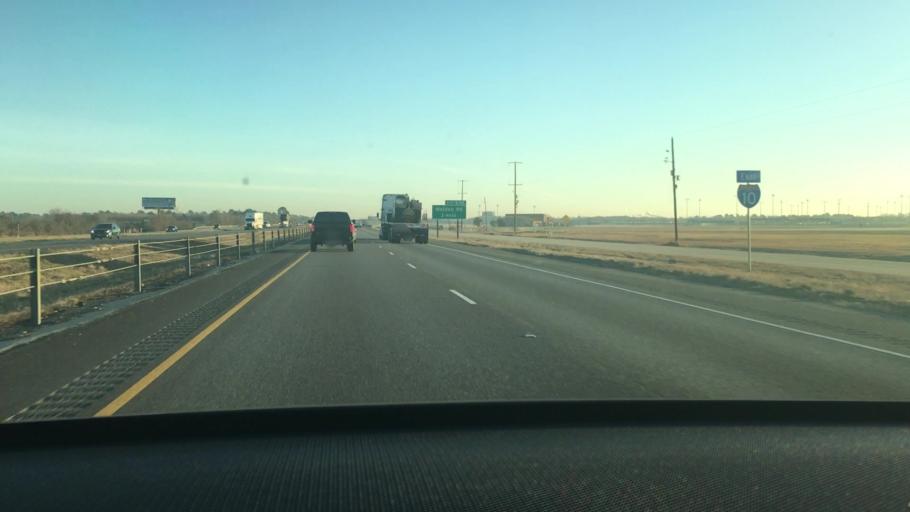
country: US
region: Texas
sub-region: Jefferson County
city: Fannett
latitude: 30.0121
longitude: -94.1835
